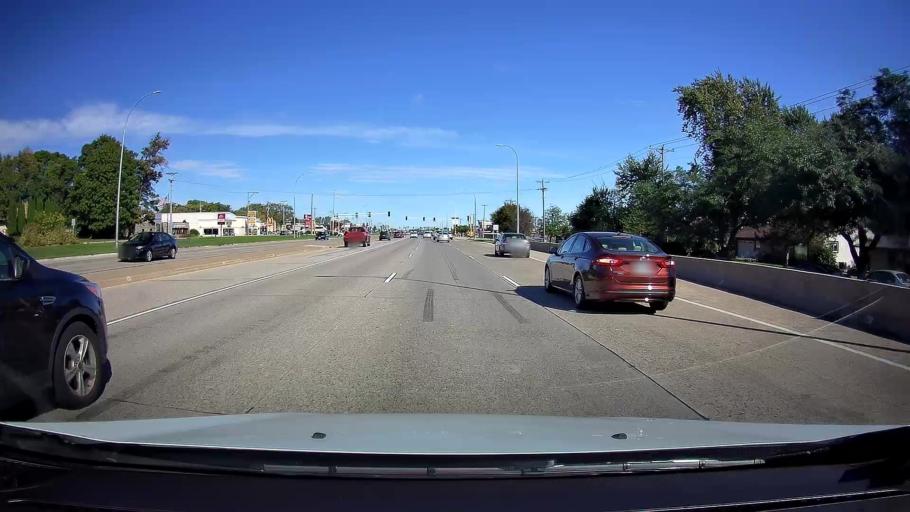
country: US
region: Minnesota
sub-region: Ramsey County
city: Falcon Heights
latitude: 45.0019
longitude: -93.1664
